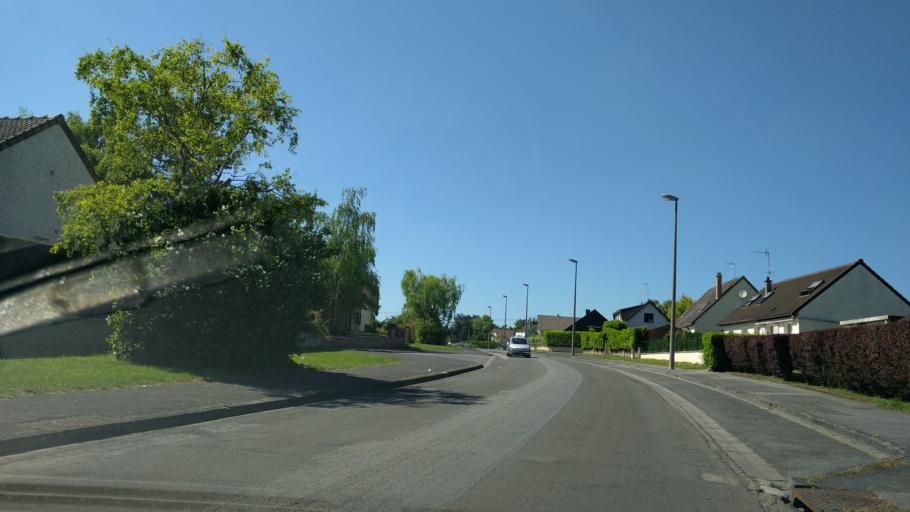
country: FR
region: Picardie
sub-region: Departement de la Somme
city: Peronne
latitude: 49.9417
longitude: 2.9367
